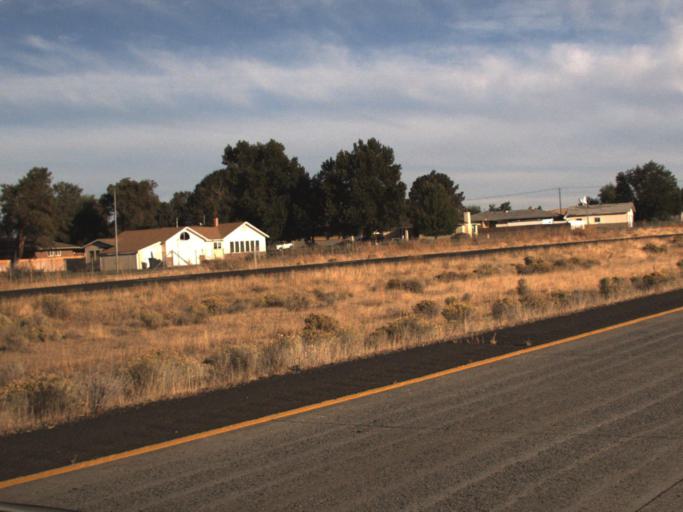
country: US
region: Washington
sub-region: Franklin County
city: Connell
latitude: 46.6577
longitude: -118.8517
